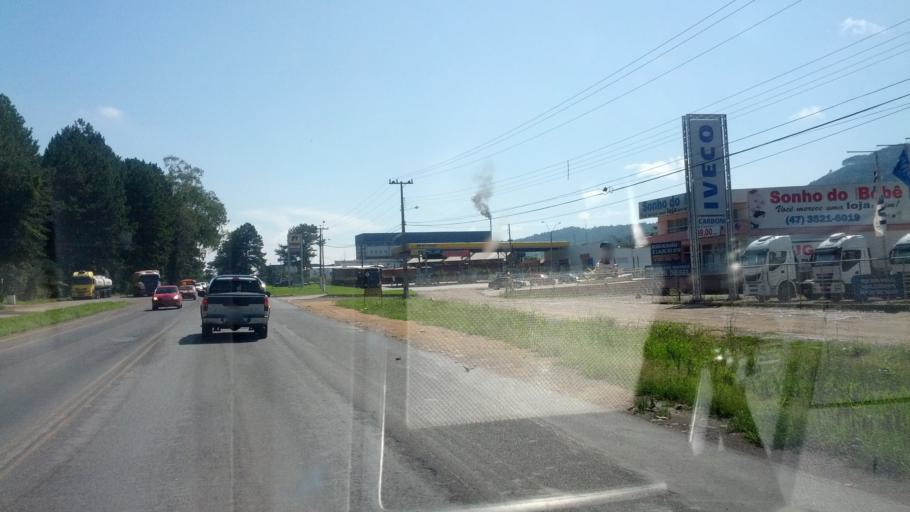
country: BR
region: Santa Catarina
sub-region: Rio Do Sul
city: Rio do Sul
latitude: -27.2432
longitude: -49.6896
